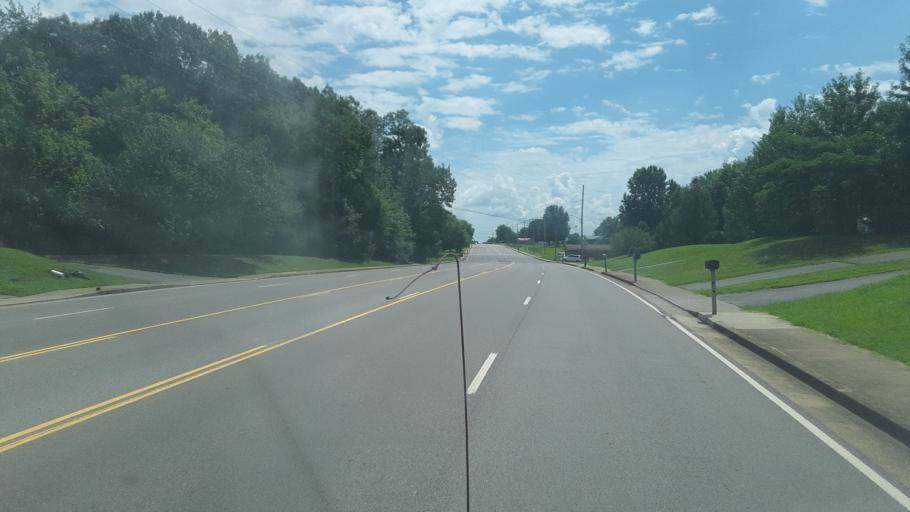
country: US
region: Kentucky
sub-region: Christian County
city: Fort Campbell North
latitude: 36.5760
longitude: -87.4427
